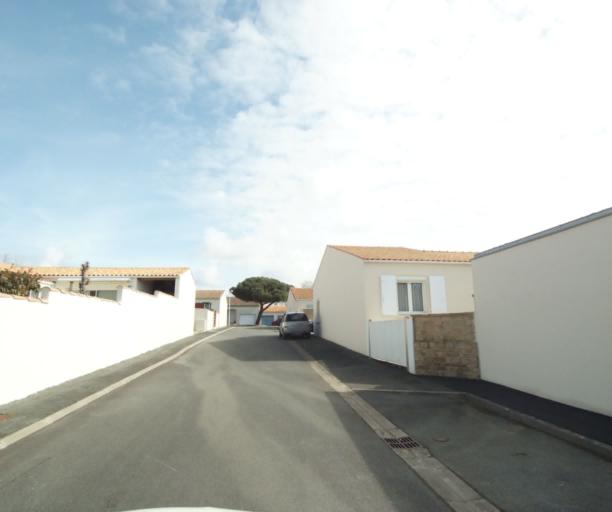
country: FR
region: Poitou-Charentes
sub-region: Departement de la Charente-Maritime
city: Lagord
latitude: 46.1819
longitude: -1.1542
